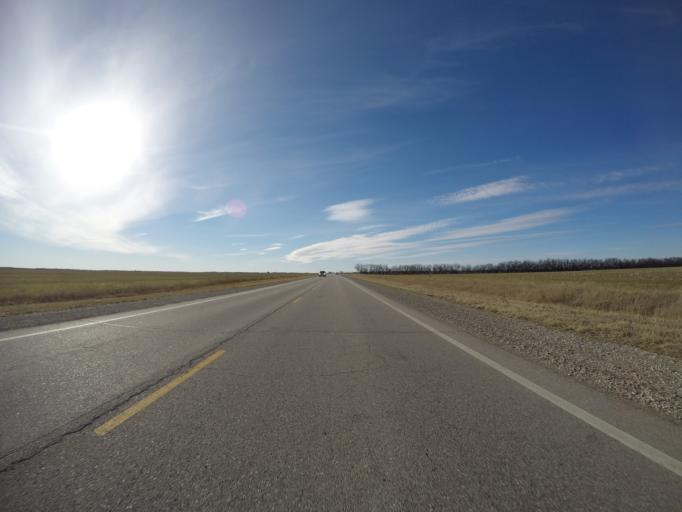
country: US
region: Kansas
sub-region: Marion County
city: Hillsboro
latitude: 38.3770
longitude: -97.4012
